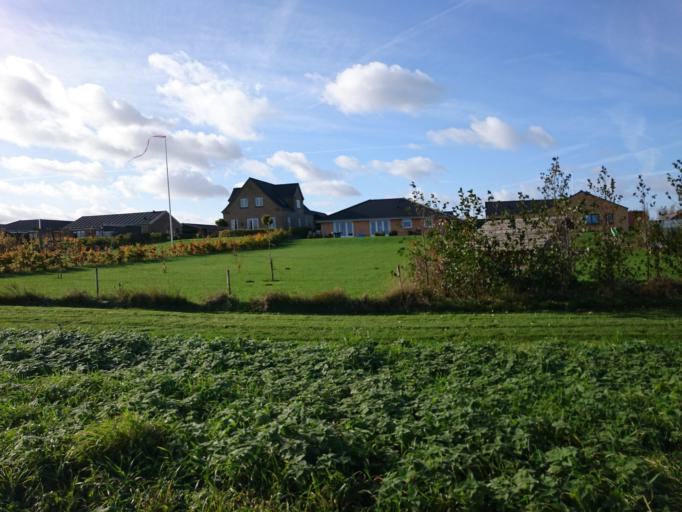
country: DK
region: South Denmark
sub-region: Odense Kommune
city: Hojby
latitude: 55.3265
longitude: 10.4334
